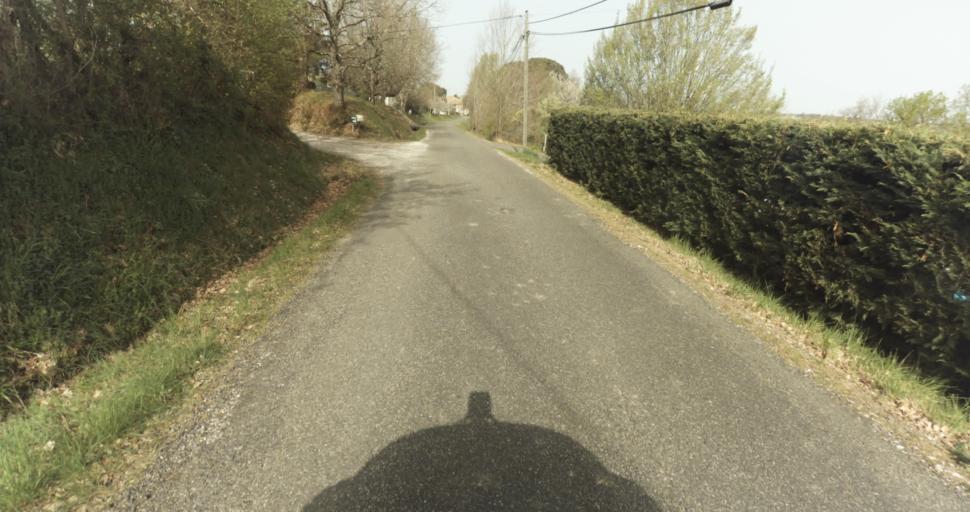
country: FR
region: Midi-Pyrenees
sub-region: Departement du Tarn-et-Garonne
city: Moissac
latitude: 44.1406
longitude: 1.0907
